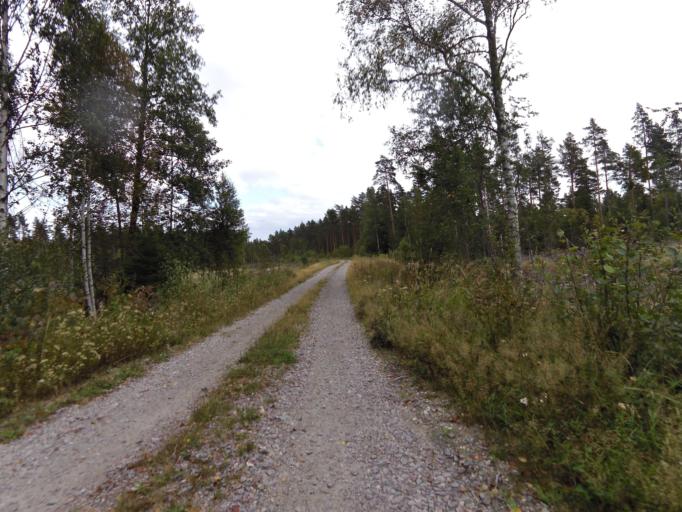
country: SE
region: Gaevleborg
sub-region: Gavle Kommun
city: Valbo
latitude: 60.7239
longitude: 17.0636
